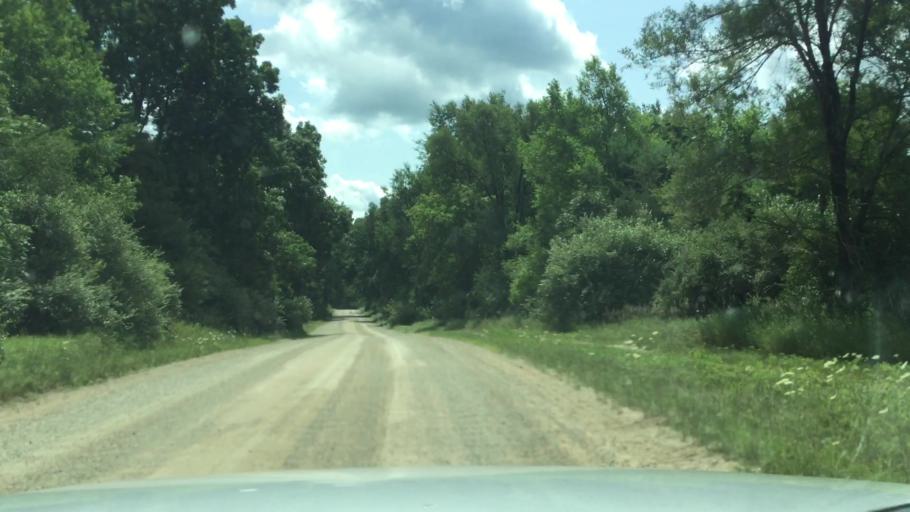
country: US
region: Michigan
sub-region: Ionia County
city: Belding
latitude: 43.1159
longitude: -85.2091
